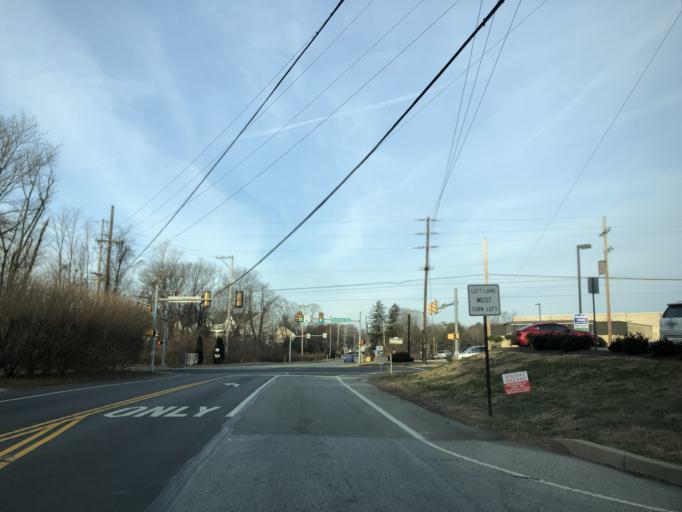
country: US
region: Pennsylvania
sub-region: Chester County
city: Exton
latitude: 40.0085
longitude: -75.5903
